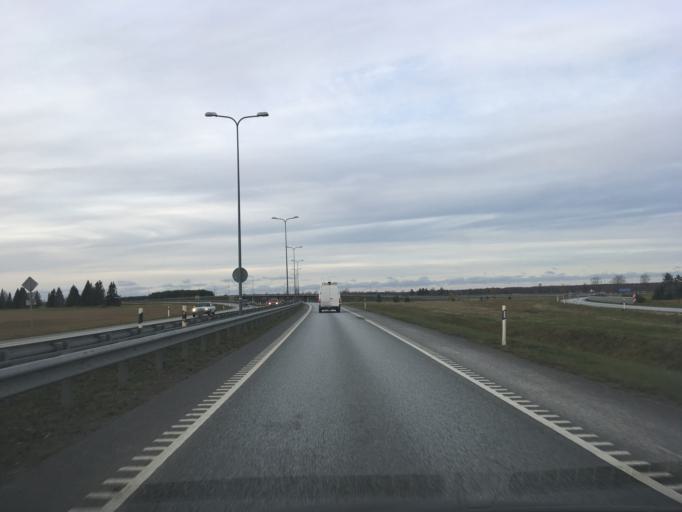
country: EE
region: Ida-Virumaa
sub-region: Kohtla-Jaerve linn
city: Kohtla-Jarve
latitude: 59.3996
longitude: 27.3315
